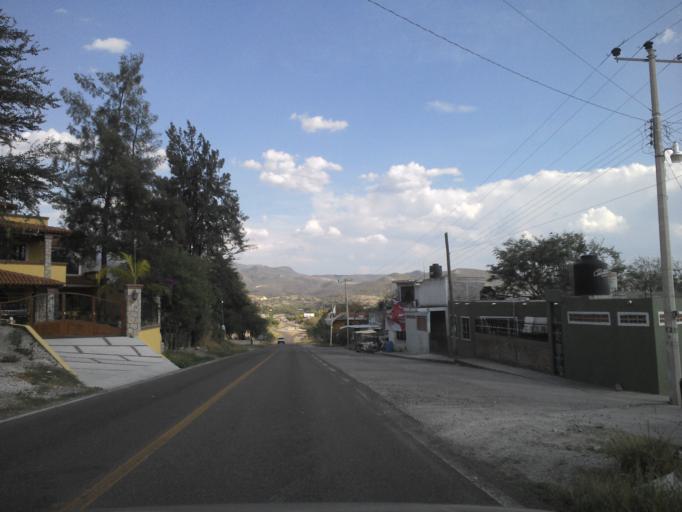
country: MX
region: Zacatecas
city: Juchipila
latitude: 21.2687
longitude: -103.1639
